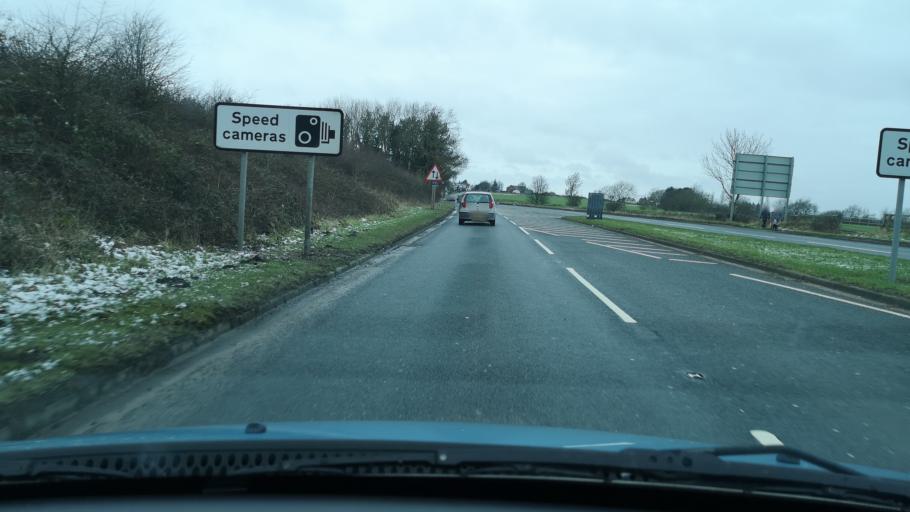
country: GB
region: England
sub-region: City and Borough of Wakefield
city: Middlestown
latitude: 53.6256
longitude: -1.5817
